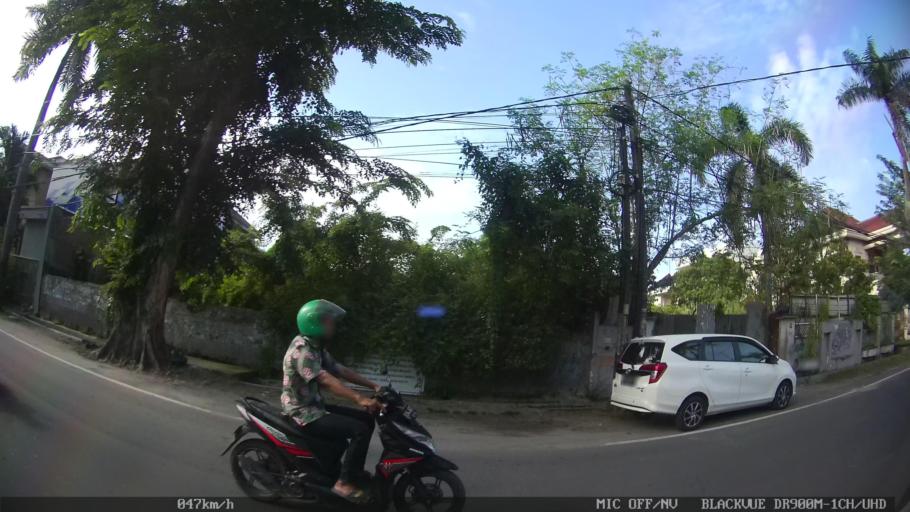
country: ID
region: North Sumatra
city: Medan
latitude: 3.6077
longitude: 98.6561
